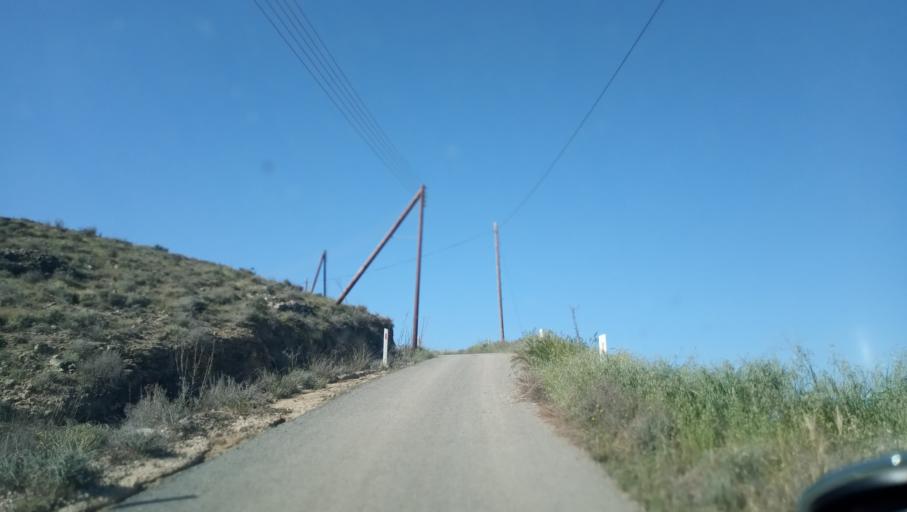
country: CY
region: Lefkosia
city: Tseri
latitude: 35.0700
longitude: 33.3150
